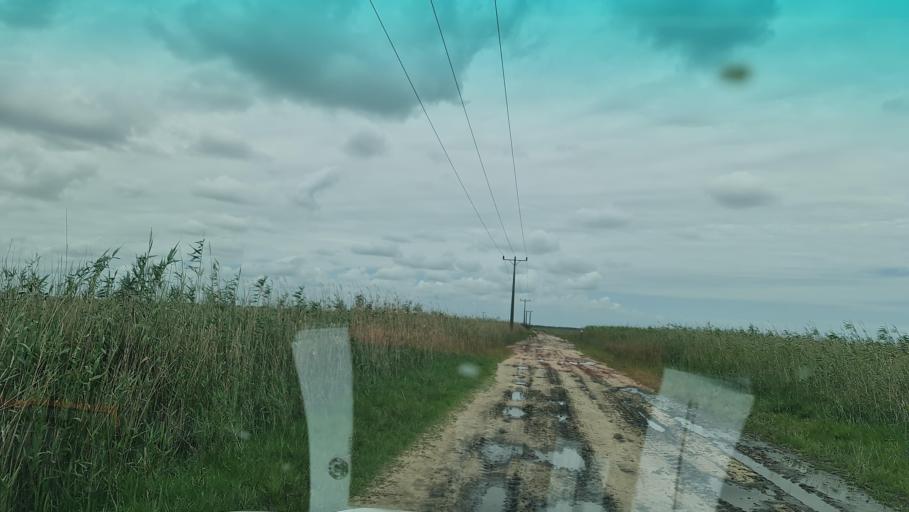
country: MZ
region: Maputo City
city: Maputo
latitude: -25.7180
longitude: 32.7010
